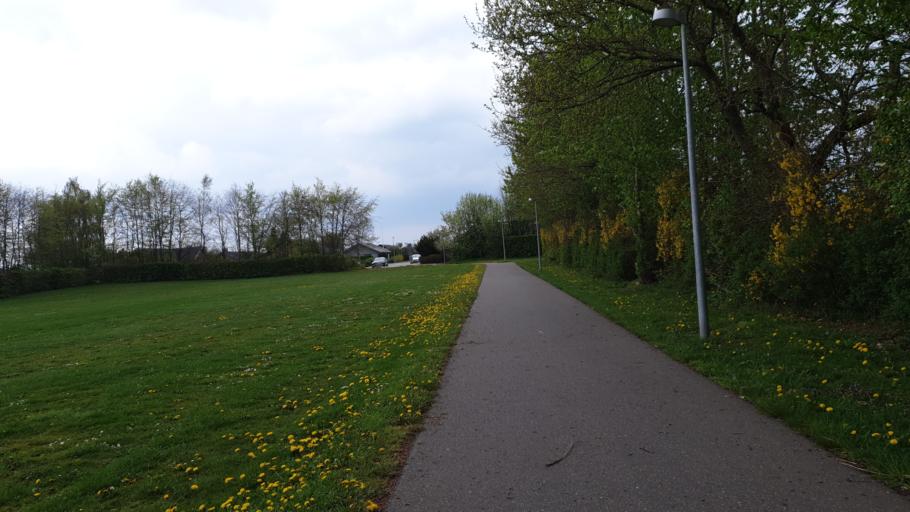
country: DK
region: Central Jutland
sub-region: Hedensted Kommune
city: Hedensted
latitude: 55.7956
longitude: 9.6918
